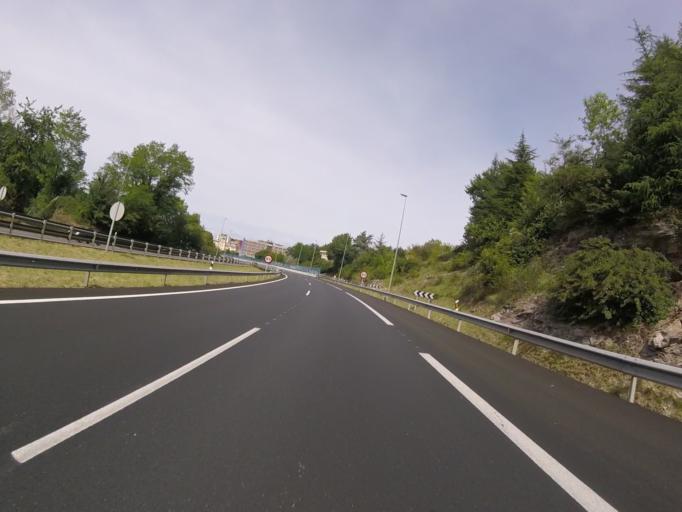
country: ES
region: Basque Country
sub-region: Provincia de Guipuzcoa
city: San Sebastian
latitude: 43.3064
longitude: -1.9681
